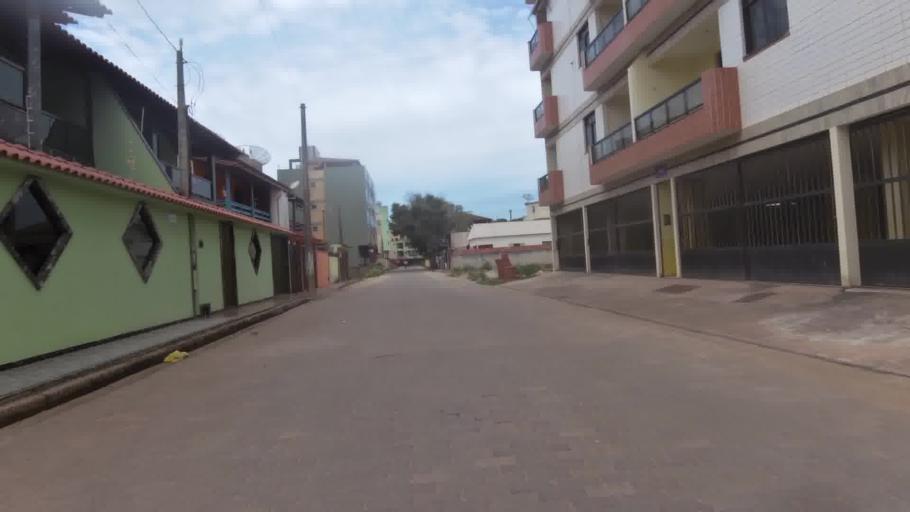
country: BR
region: Espirito Santo
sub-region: Piuma
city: Piuma
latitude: -20.8447
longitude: -40.7449
